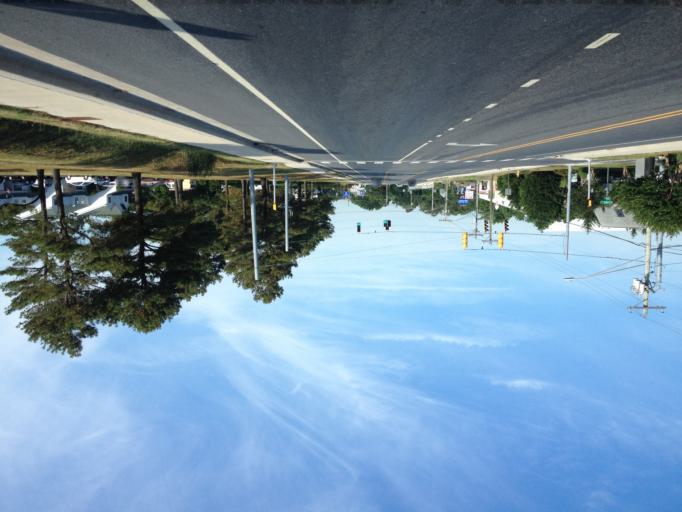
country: US
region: Delaware
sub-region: Sussex County
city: Ocean View
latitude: 38.4658
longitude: -75.0867
